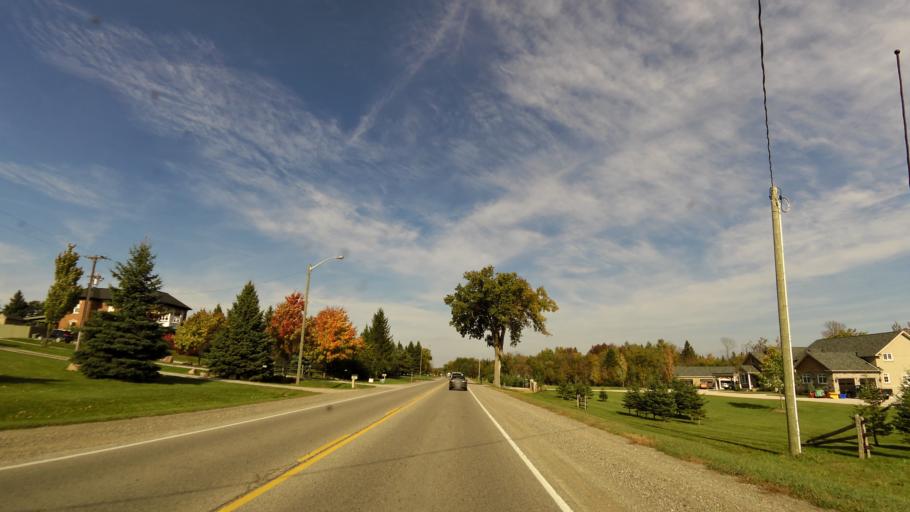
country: CA
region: Ontario
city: Orangeville
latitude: 43.7576
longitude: -80.0635
